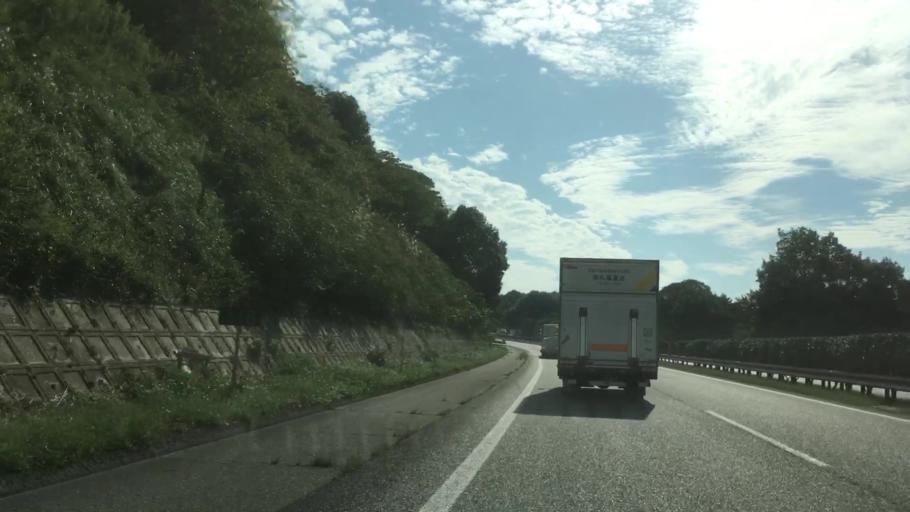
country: JP
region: Yamaguchi
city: Yanai
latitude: 34.0785
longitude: 132.0720
